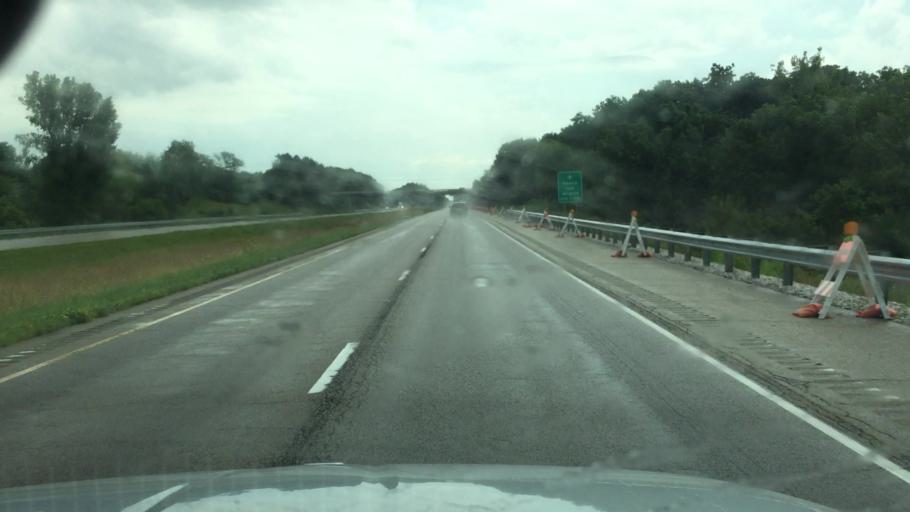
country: US
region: Illinois
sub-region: Peoria County
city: Bellevue
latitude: 40.7492
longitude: -89.6905
